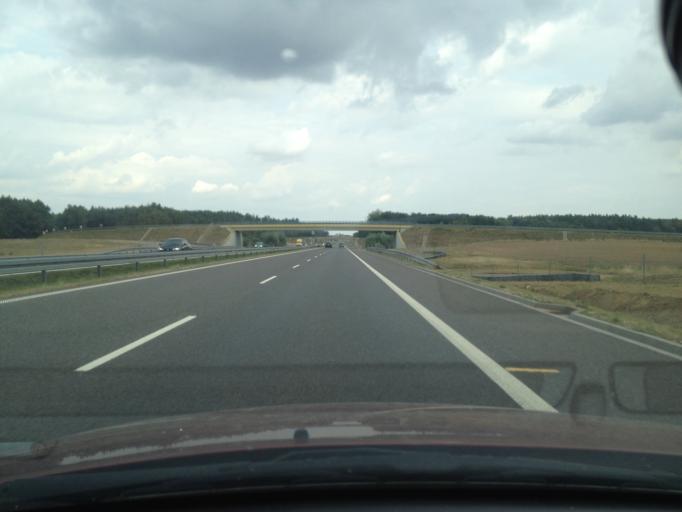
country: PL
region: West Pomeranian Voivodeship
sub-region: Powiat mysliborski
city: Mysliborz
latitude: 53.0054
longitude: 14.8620
